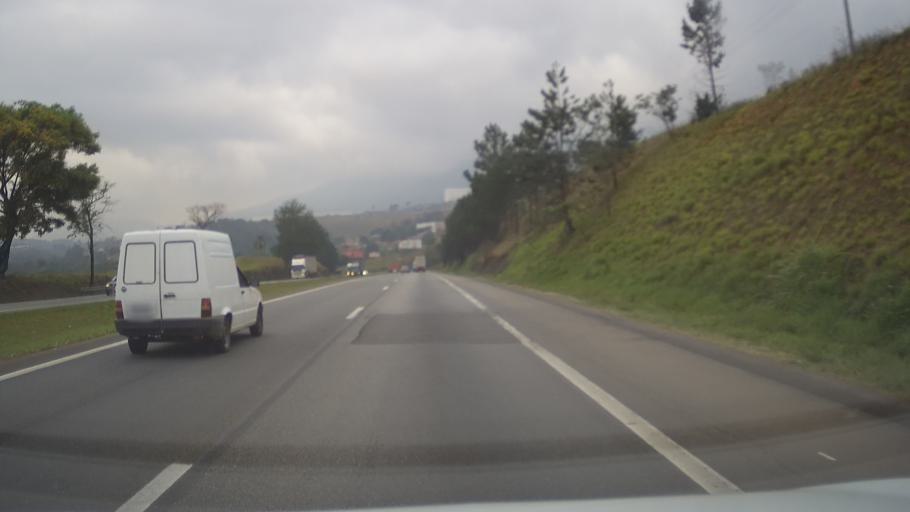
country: BR
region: Minas Gerais
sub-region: Extrema
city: Extrema
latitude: -22.8815
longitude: -46.3799
